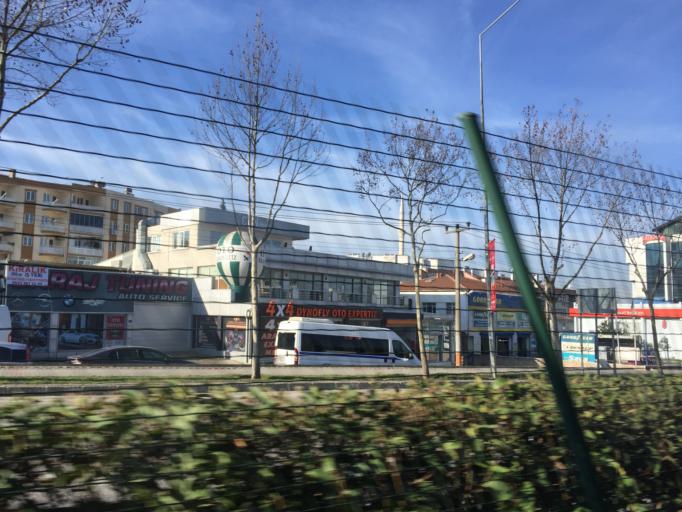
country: TR
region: Bursa
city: Niluefer
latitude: 40.2354
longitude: 28.9776
